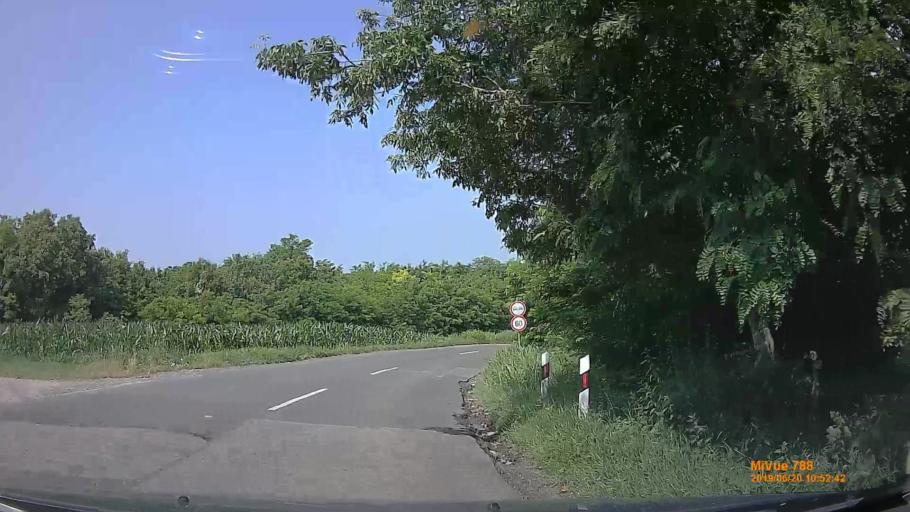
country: HU
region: Baranya
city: Mecseknadasd
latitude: 46.1549
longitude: 18.5777
